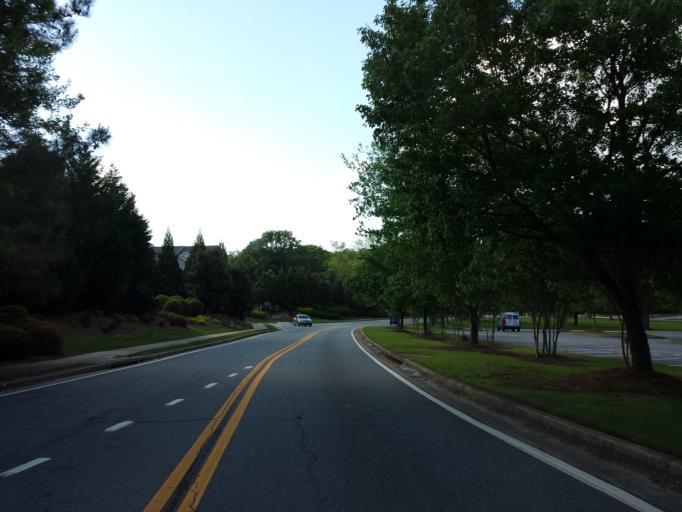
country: US
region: Georgia
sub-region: Cobb County
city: Marietta
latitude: 33.9350
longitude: -84.5455
